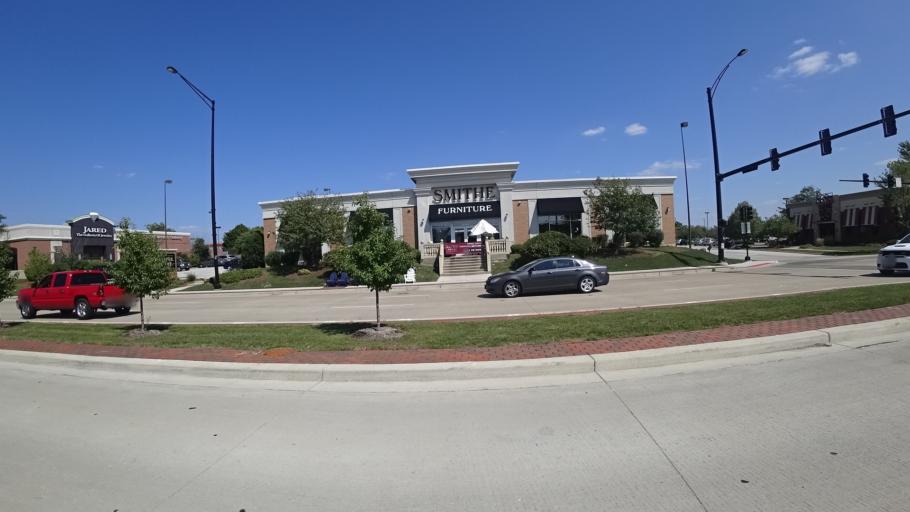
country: US
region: Illinois
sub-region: Cook County
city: Orland Park
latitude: 41.6105
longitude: -87.8533
